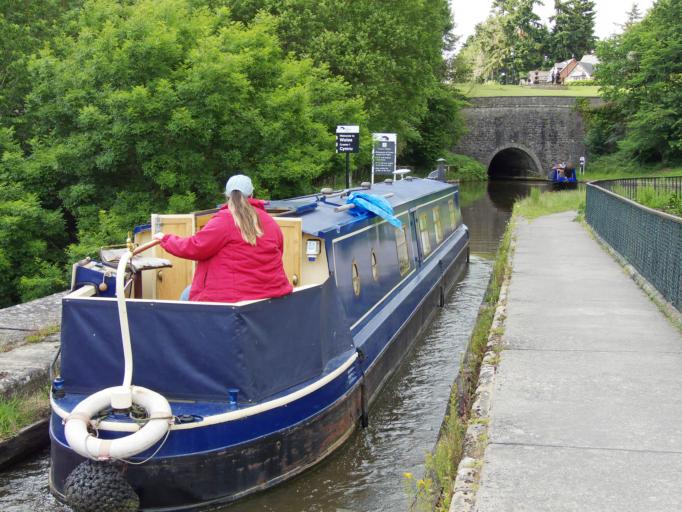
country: GB
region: Wales
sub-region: Wrexham
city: Chirk
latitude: 52.9281
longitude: -3.0621
